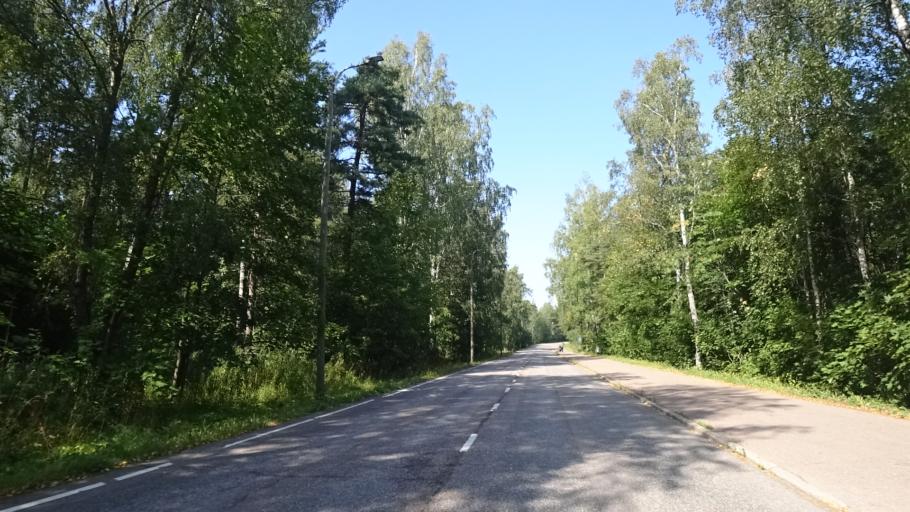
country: FI
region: Kymenlaakso
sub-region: Kotka-Hamina
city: Karhula
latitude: 60.5032
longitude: 26.9502
